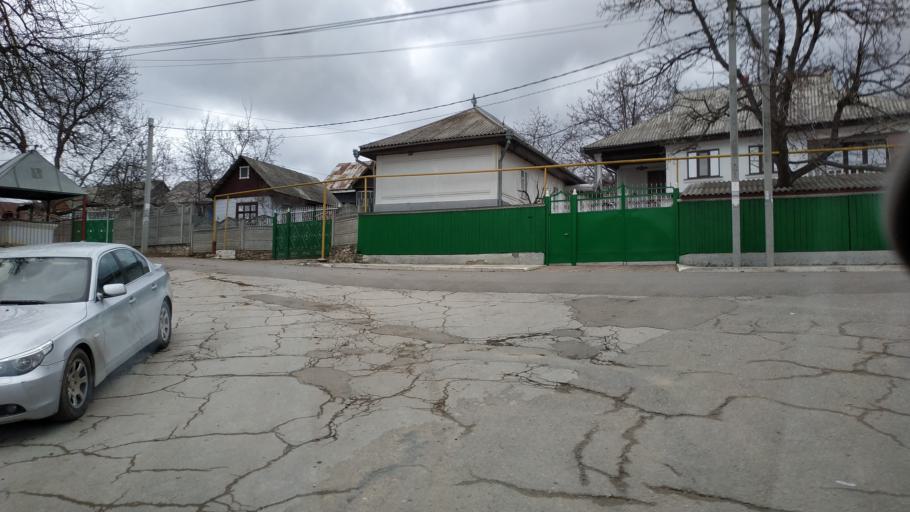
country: MD
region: Calarasi
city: Calarasi
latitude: 47.2106
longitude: 28.2495
